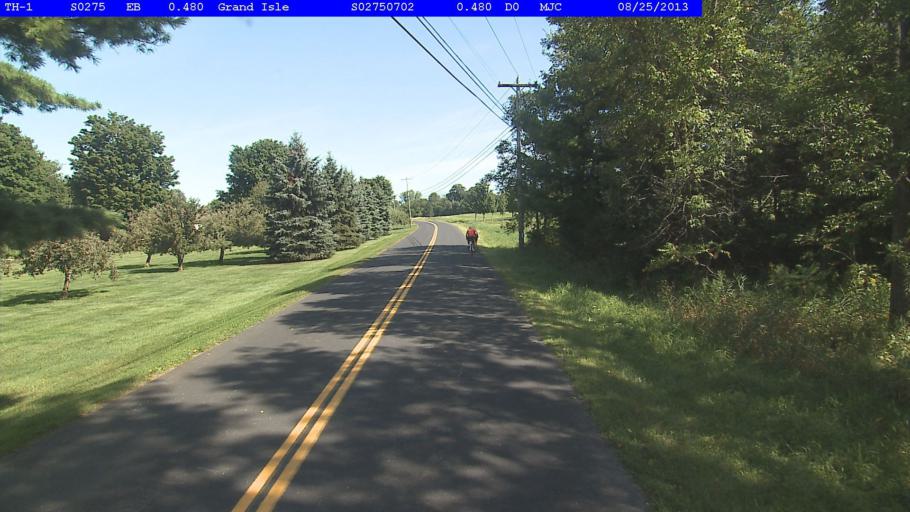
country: US
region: New York
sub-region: Clinton County
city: Cumberland Head
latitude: 44.7074
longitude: -73.3436
